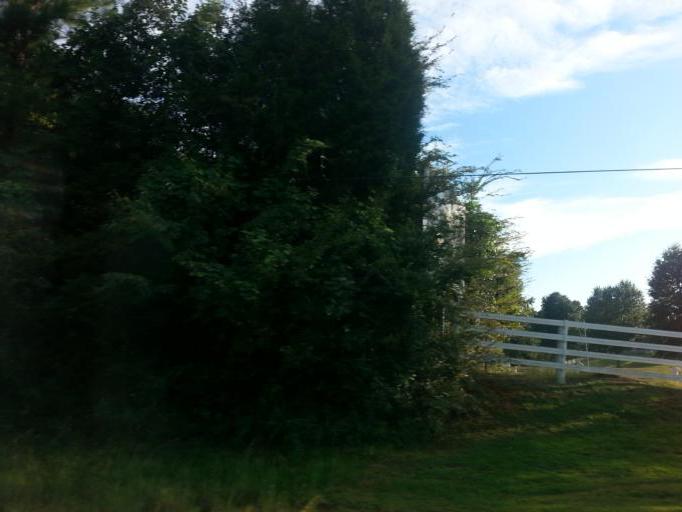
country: US
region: Alabama
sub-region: Lauderdale County
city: Rogersville
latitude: 34.8523
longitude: -87.4040
